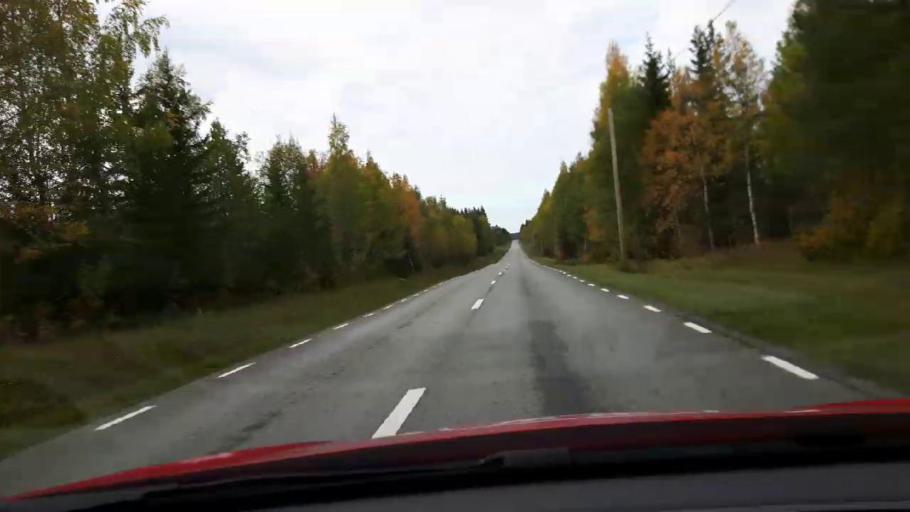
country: SE
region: Jaemtland
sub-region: Krokoms Kommun
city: Krokom
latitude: 63.1914
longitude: 14.0580
